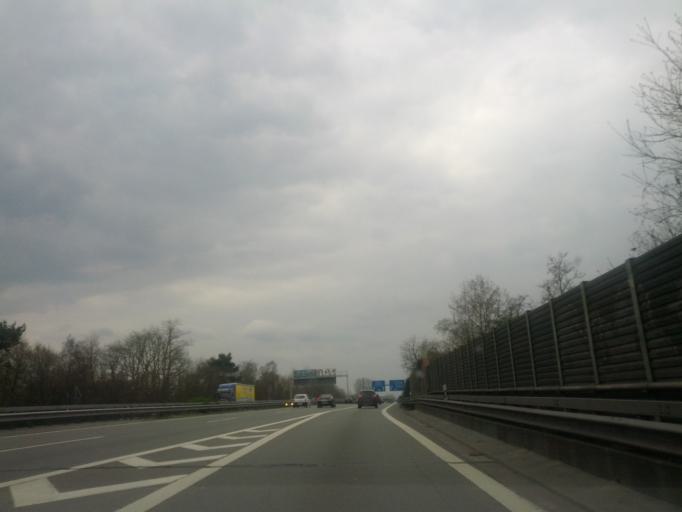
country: DE
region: Lower Saxony
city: Oldenburg
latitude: 53.1514
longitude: 8.1935
